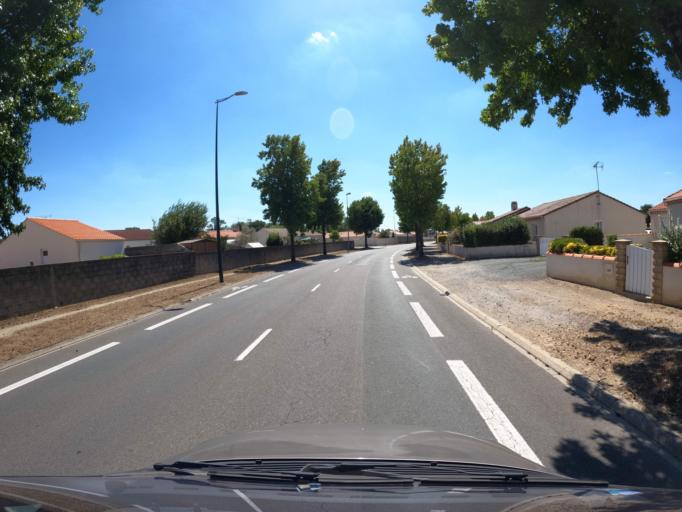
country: FR
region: Pays de la Loire
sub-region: Departement de la Vendee
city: Challans
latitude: 46.8445
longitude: -1.8593
